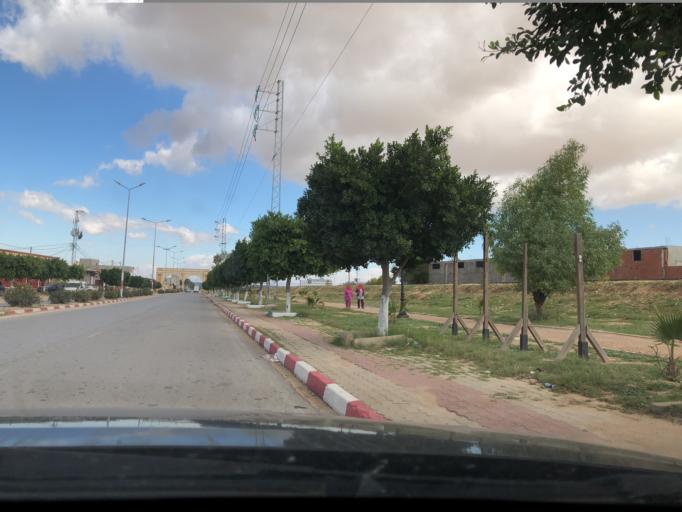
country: TN
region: Al Qasrayn
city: Kasserine
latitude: 35.1808
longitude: 8.8569
